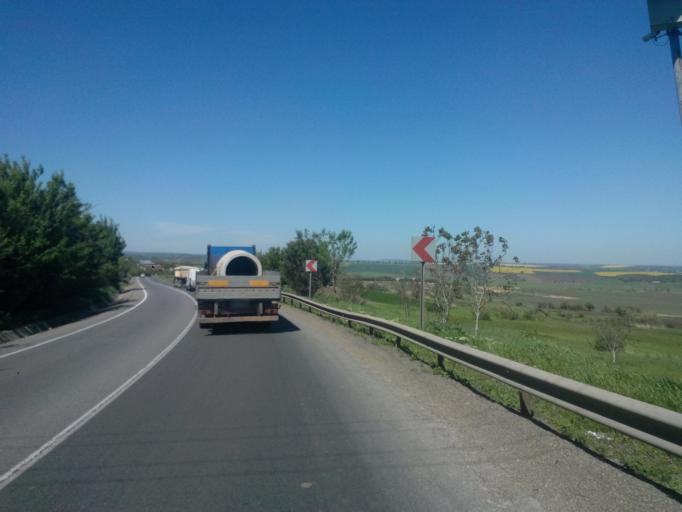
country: RO
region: Iasi
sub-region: Comuna Strunga
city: Strunga
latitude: 47.1714
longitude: 26.9550
